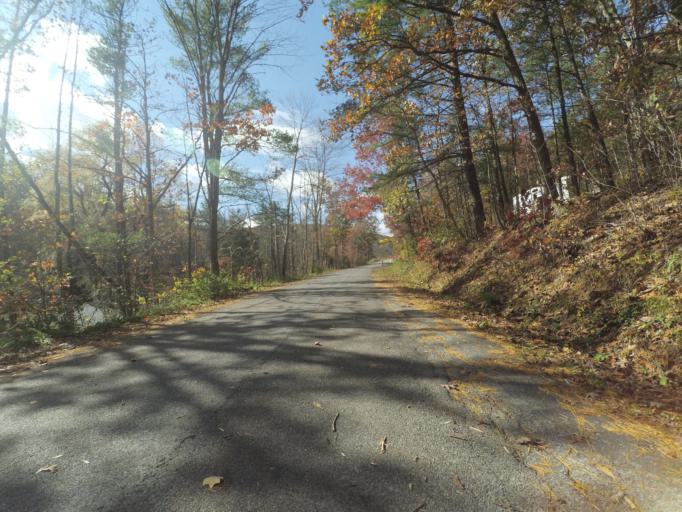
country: US
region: Pennsylvania
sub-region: Centre County
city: Park Forest Village
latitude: 40.8614
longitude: -77.9618
